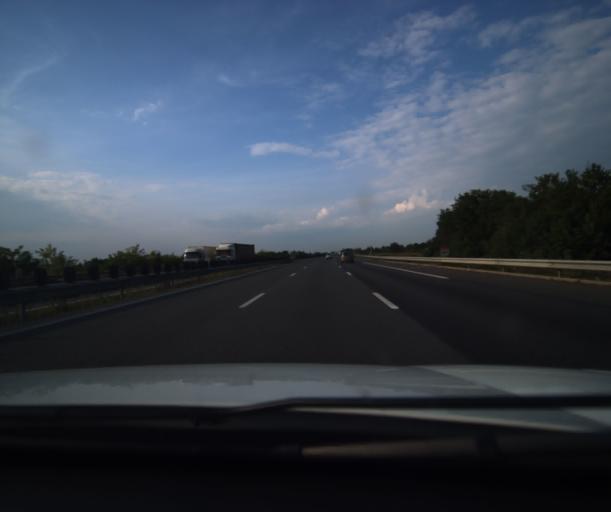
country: FR
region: Midi-Pyrenees
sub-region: Departement du Tarn-et-Garonne
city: Campsas
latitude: 43.9033
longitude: 1.3167
